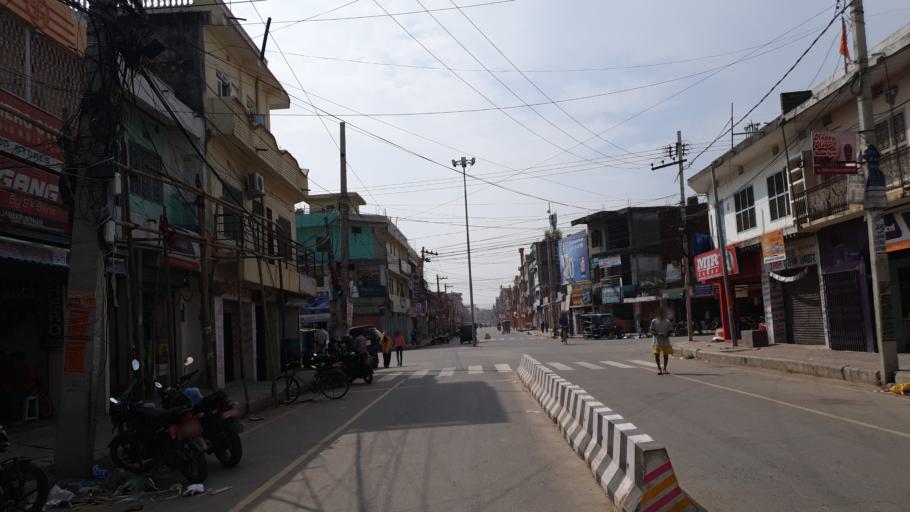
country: NP
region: Central Region
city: Janakpur
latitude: 26.7321
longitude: 85.9336
